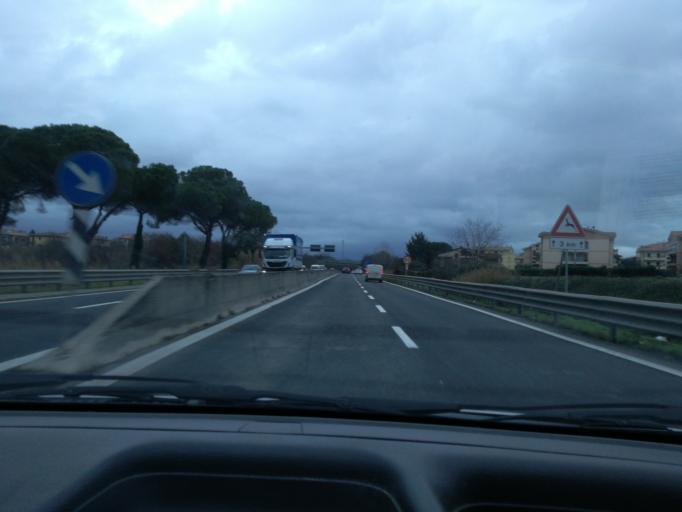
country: IT
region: Umbria
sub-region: Provincia di Perugia
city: Via Lippia
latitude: 43.0877
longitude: 12.4767
